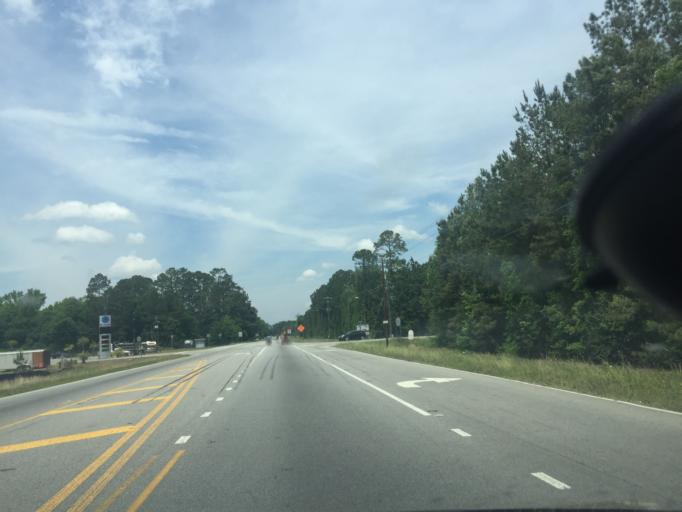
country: US
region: Georgia
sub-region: Chatham County
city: Bloomingdale
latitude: 32.1839
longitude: -81.3996
